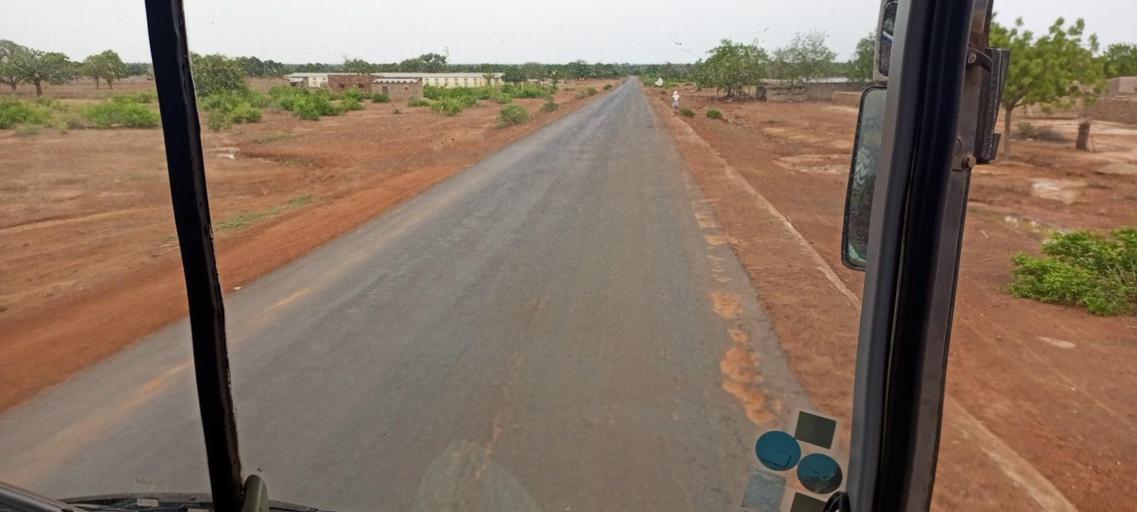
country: ML
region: Segou
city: Bla
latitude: 12.6887
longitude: -5.7237
